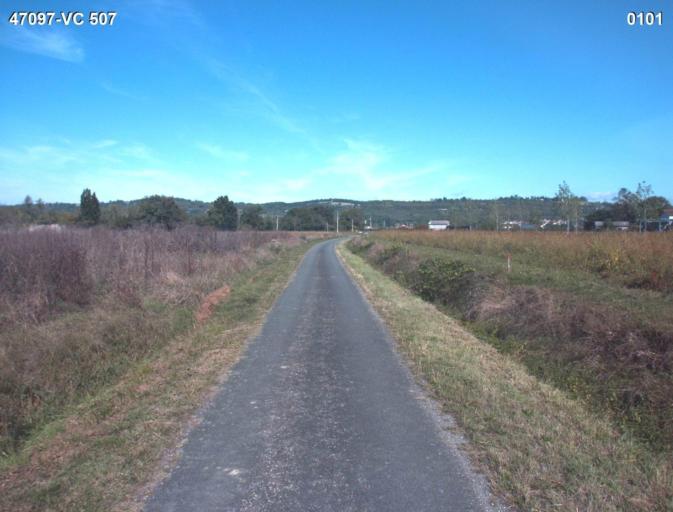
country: FR
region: Aquitaine
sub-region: Departement du Lot-et-Garonne
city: Port-Sainte-Marie
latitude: 44.2371
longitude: 0.3891
